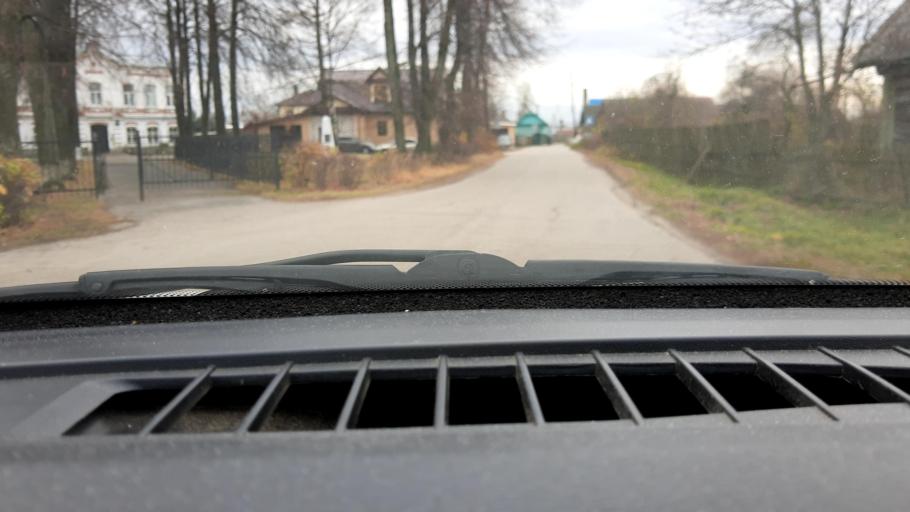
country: RU
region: Nizjnij Novgorod
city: Gorodets
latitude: 56.6377
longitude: 43.4699
